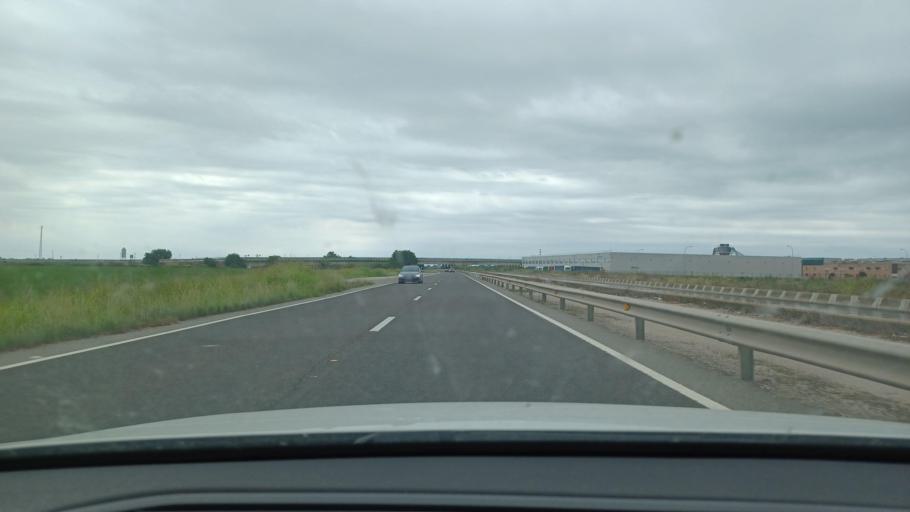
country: ES
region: Catalonia
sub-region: Provincia de Tarragona
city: Amposta
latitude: 40.7168
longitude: 0.5890
